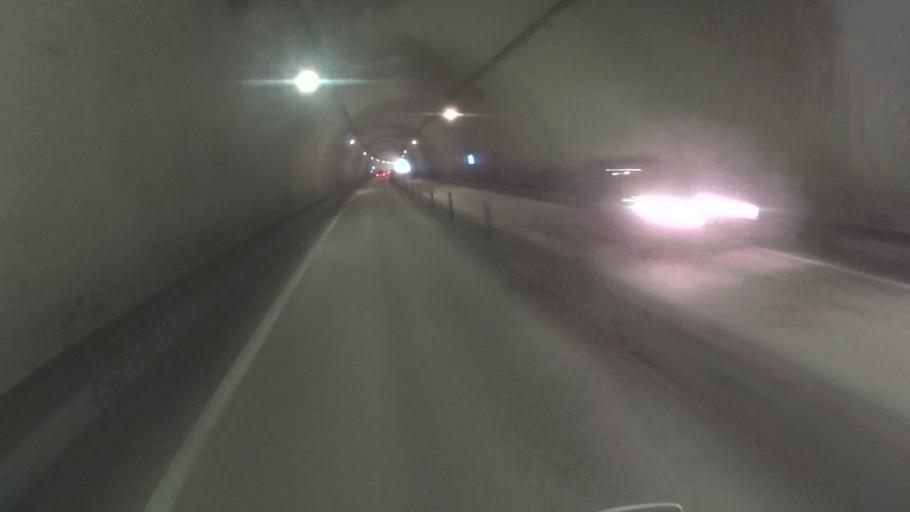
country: JP
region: Kyoto
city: Miyazu
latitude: 35.5460
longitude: 135.1520
